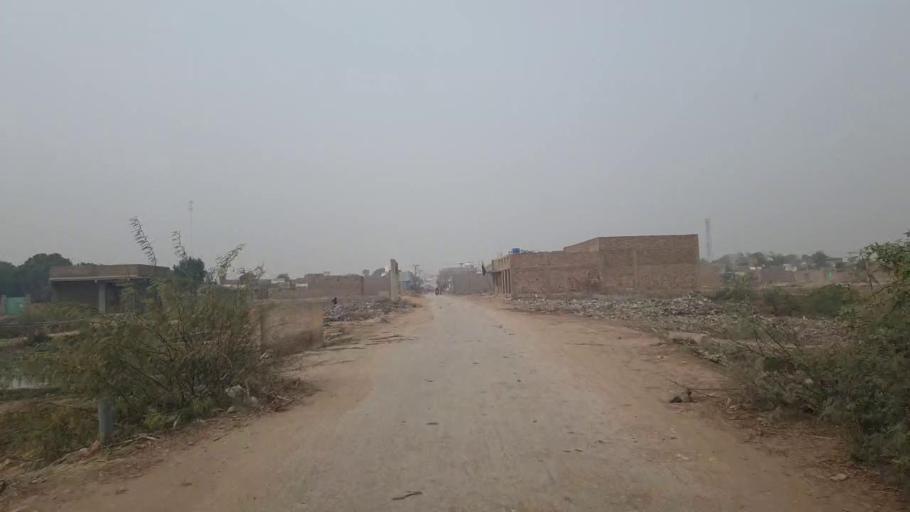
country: PK
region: Sindh
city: Tando Adam
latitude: 25.7520
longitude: 68.6687
